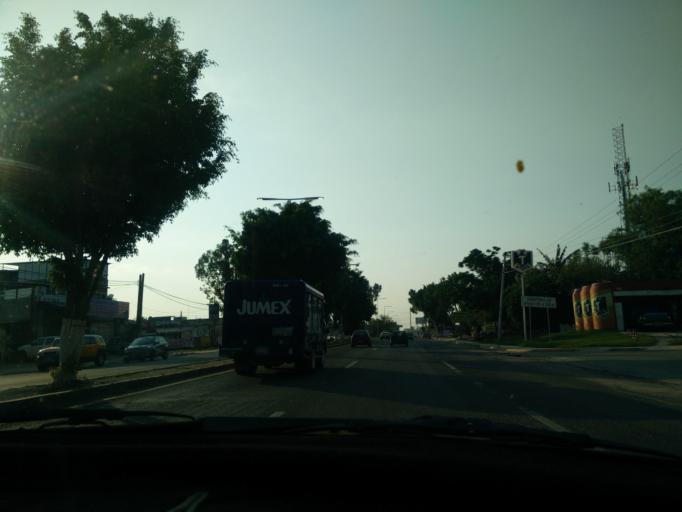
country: MX
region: Oaxaca
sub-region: Santa Maria Atzompa
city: San Jeronimo Yahuiche
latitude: 17.1198
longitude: -96.7620
